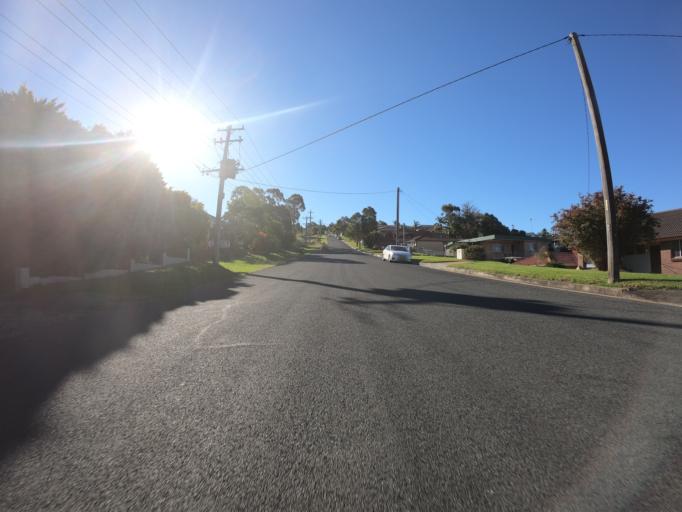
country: AU
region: New South Wales
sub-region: Wollongong
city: Cordeaux Heights
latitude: -34.4294
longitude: 150.8429
